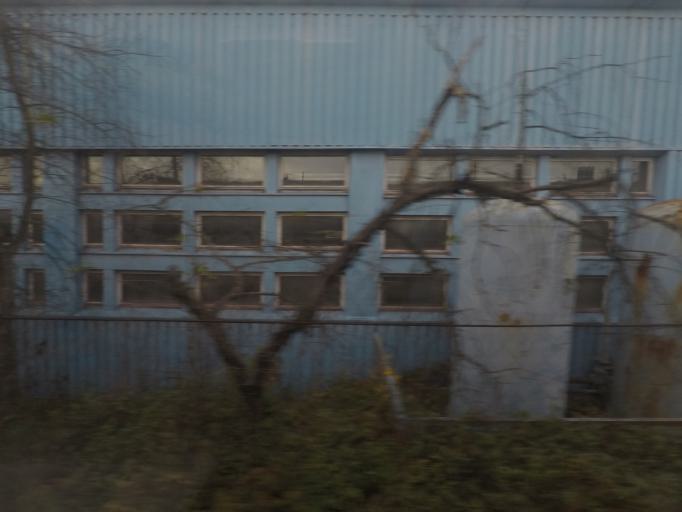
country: PL
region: Subcarpathian Voivodeship
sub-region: Powiat przemyski
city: Medyka
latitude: 49.7980
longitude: 22.9062
